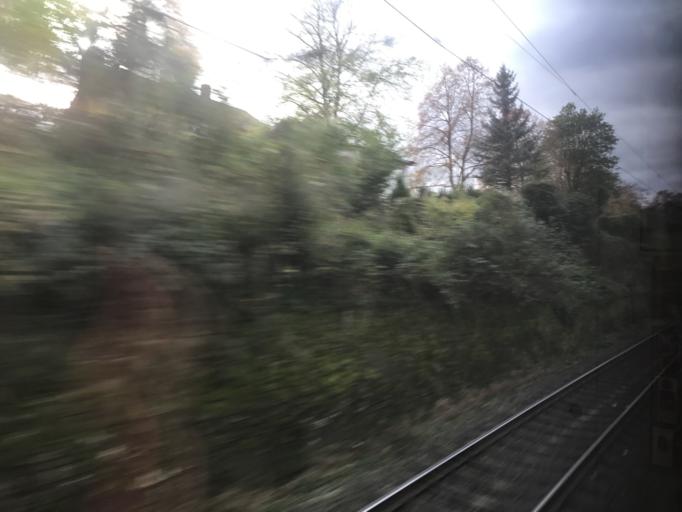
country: DE
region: North Rhine-Westphalia
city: Wetter (Ruhr)
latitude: 51.3829
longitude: 7.3969
